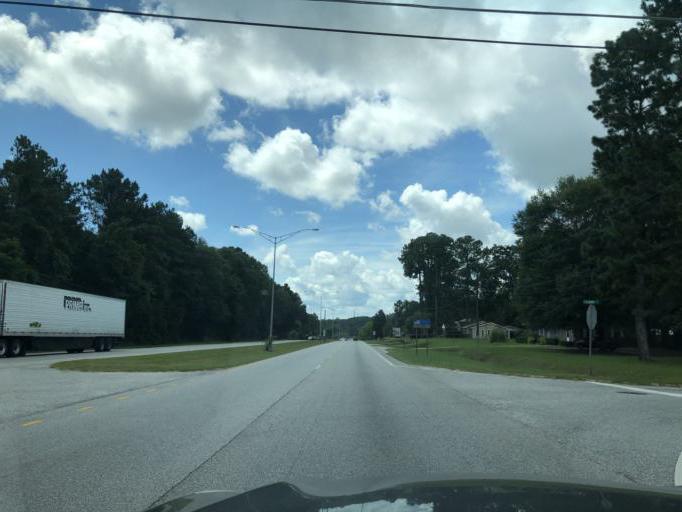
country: US
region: Alabama
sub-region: Barbour County
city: Eufaula
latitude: 31.9164
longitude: -85.1479
